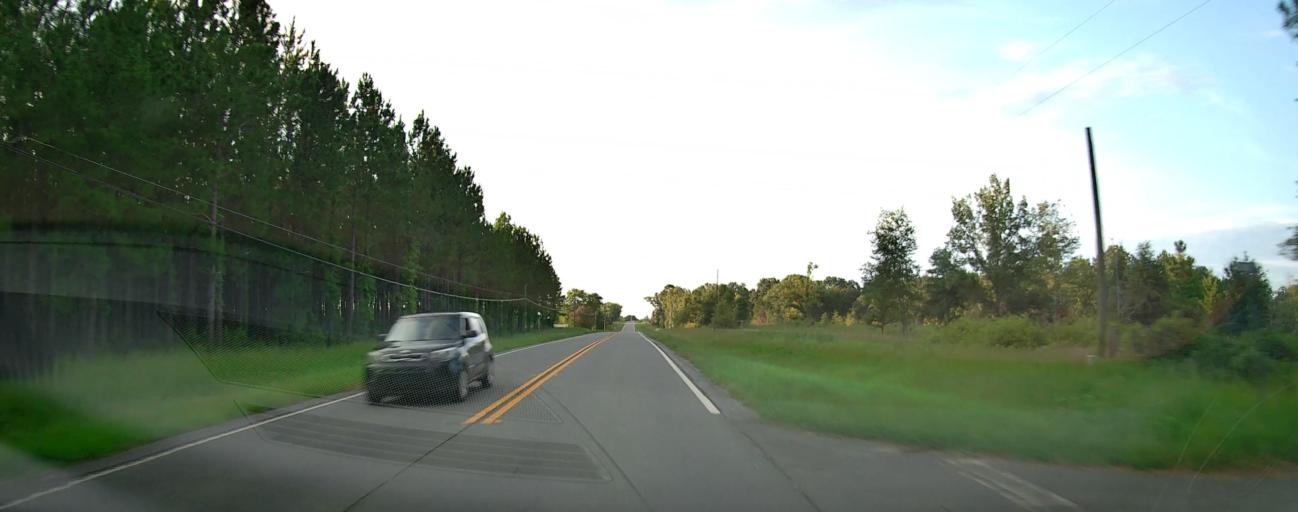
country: US
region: Georgia
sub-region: Taylor County
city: Reynolds
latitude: 32.5798
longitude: -84.0897
